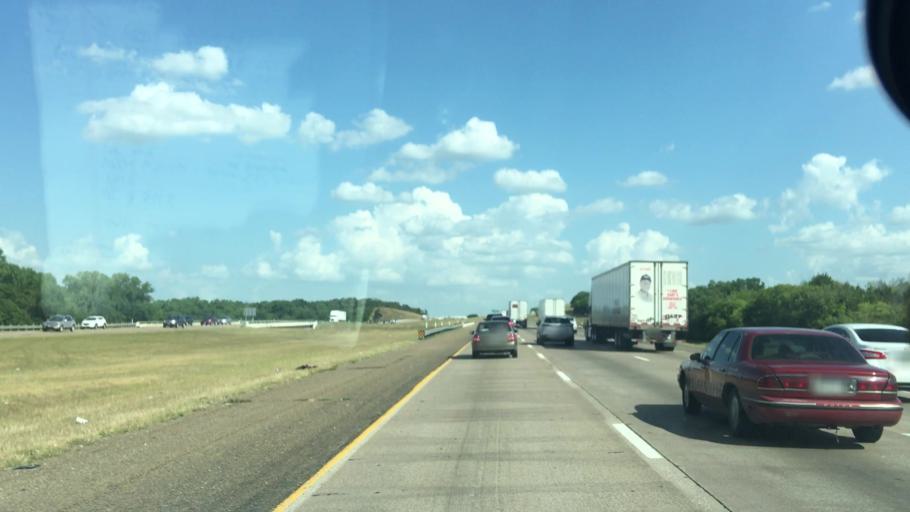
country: US
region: Texas
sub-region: Dallas County
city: Hutchins
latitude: 32.6755
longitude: -96.7391
